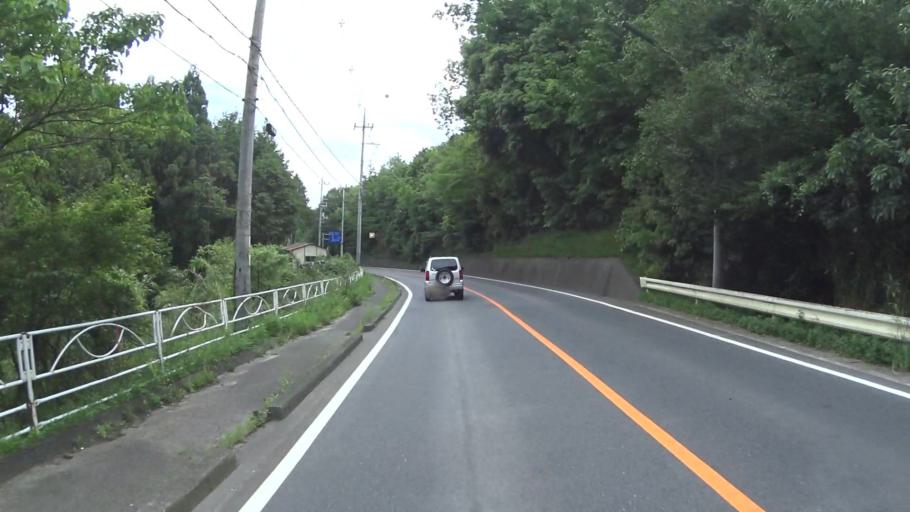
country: JP
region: Shiga Prefecture
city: Kitahama
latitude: 35.1529
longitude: 135.8761
